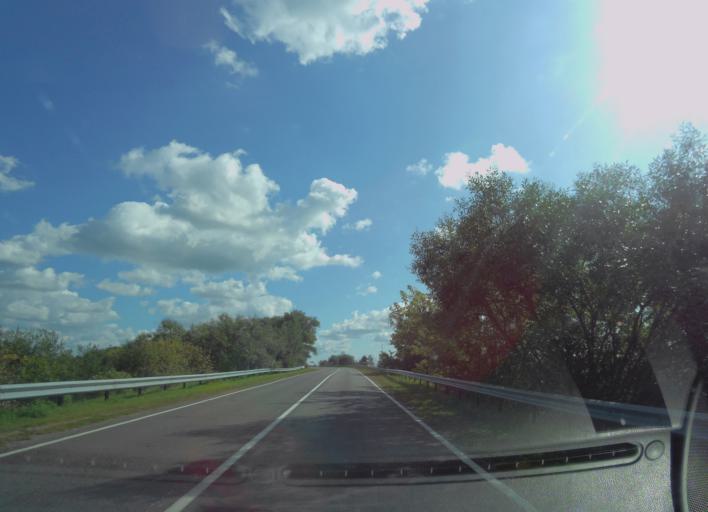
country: BY
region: Minsk
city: Zyembin
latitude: 54.3578
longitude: 28.3301
